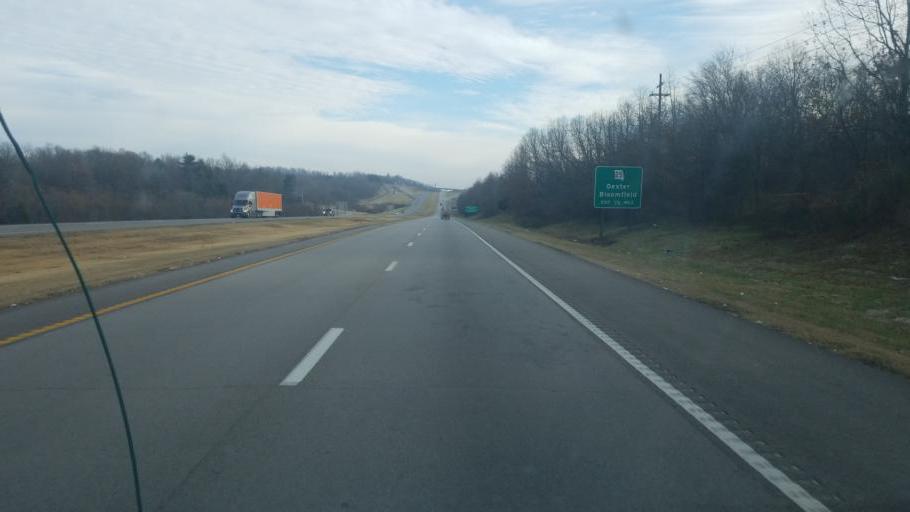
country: US
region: Missouri
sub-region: Stoddard County
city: Dexter
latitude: 36.8126
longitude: -89.9565
